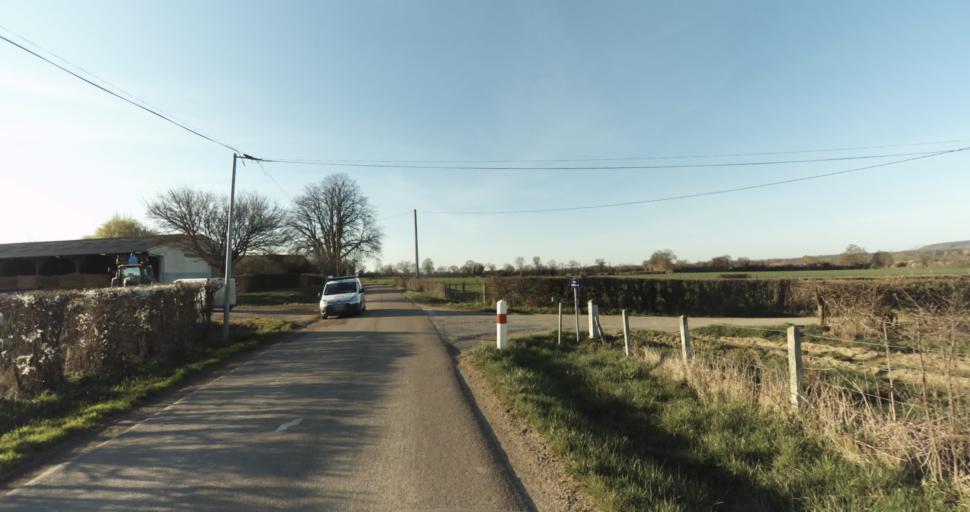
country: FR
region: Lower Normandy
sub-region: Departement du Calvados
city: Saint-Pierre-sur-Dives
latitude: 48.9572
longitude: 0.0079
